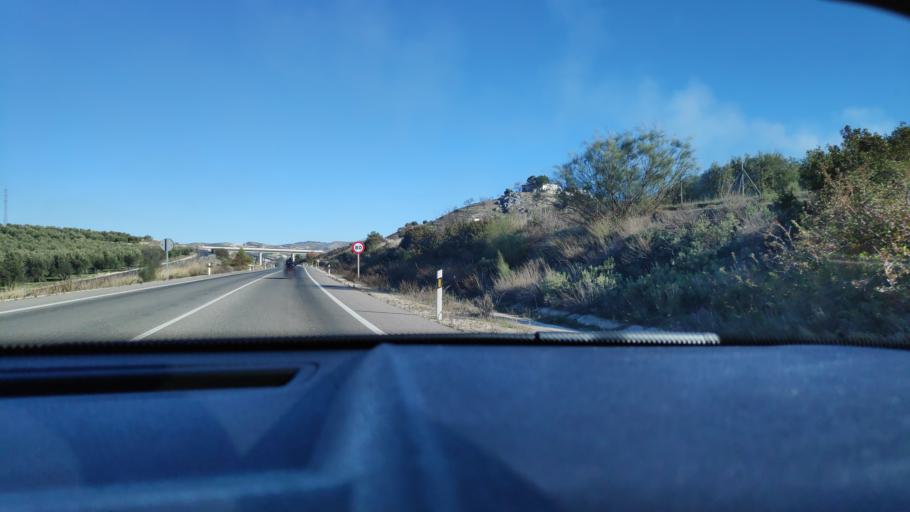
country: ES
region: Andalusia
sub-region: Province of Cordoba
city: Baena
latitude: 37.6049
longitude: -4.3033
